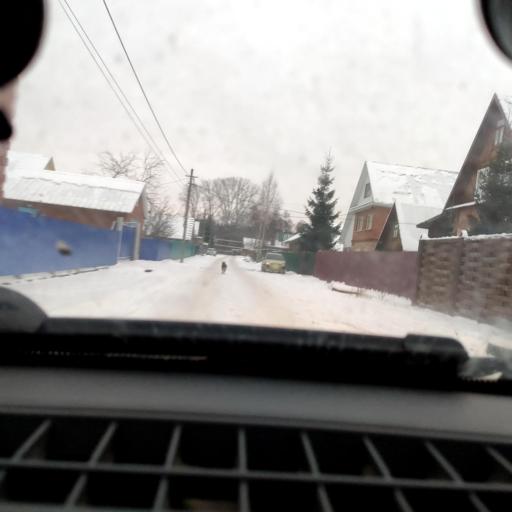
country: RU
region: Bashkortostan
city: Iglino
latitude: 54.8403
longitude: 56.2052
